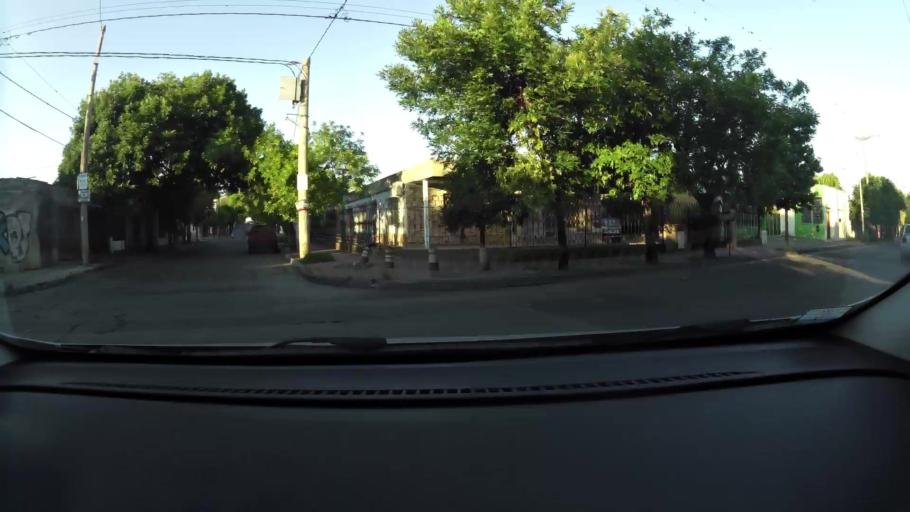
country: AR
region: Cordoba
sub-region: Departamento de Capital
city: Cordoba
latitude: -31.3845
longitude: -64.2155
